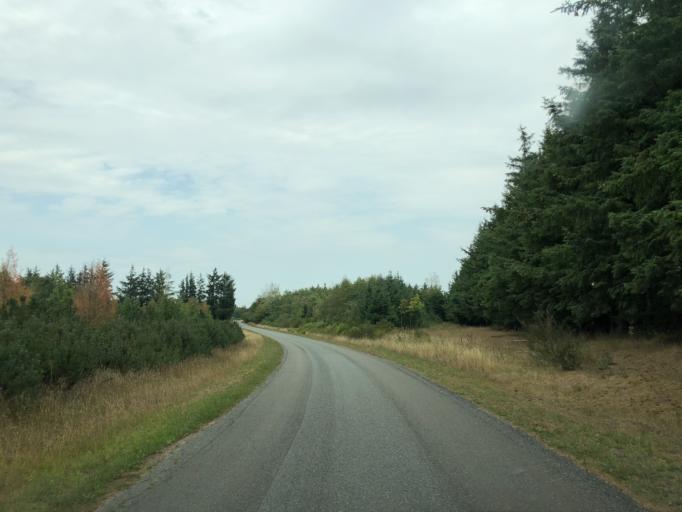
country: DK
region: Central Jutland
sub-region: Holstebro Kommune
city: Ulfborg
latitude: 56.2232
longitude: 8.3247
